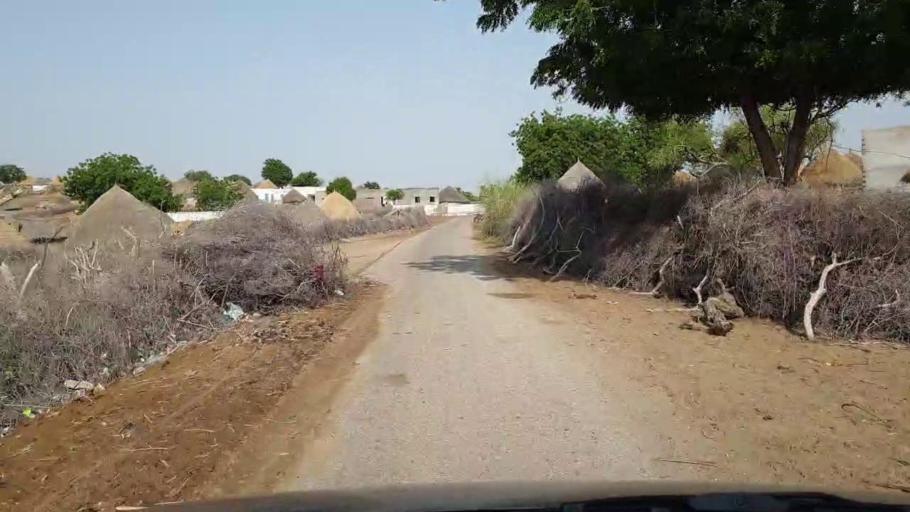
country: PK
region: Sindh
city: Chor
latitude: 25.4541
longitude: 70.5201
